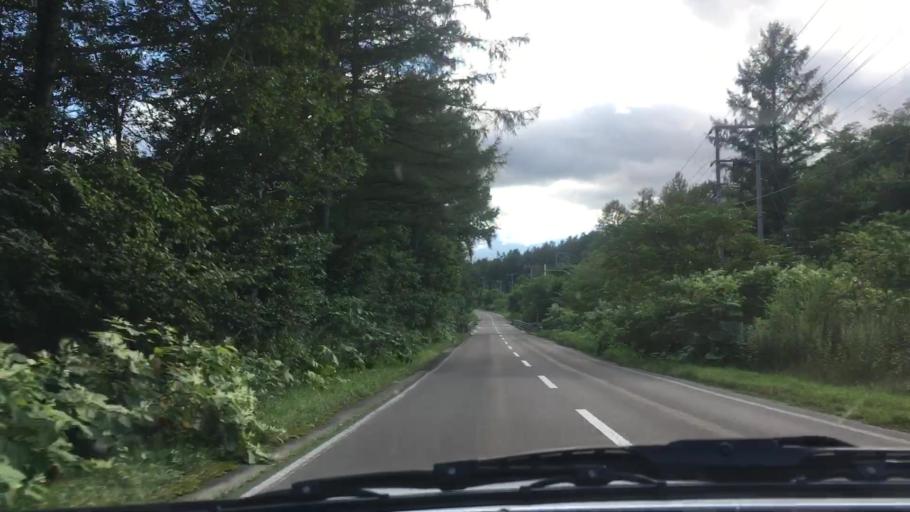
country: JP
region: Hokkaido
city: Otofuke
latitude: 43.1727
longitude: 142.9162
